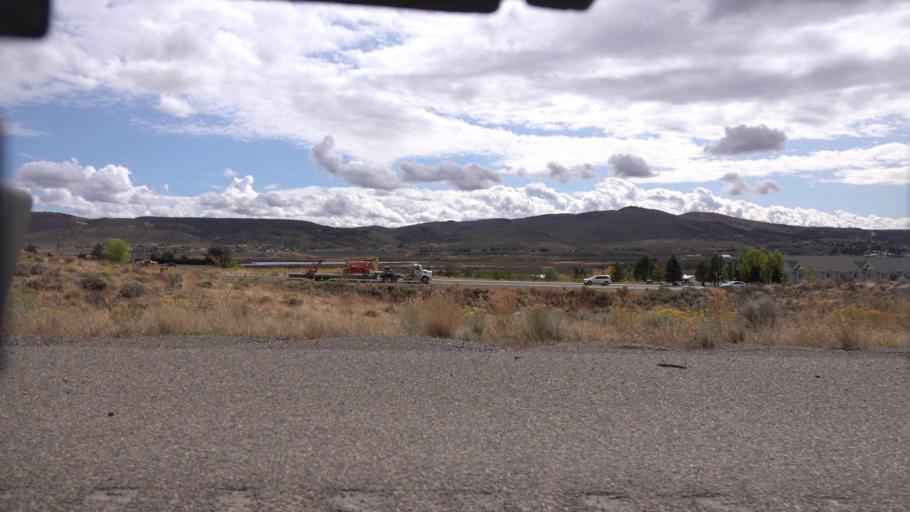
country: US
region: Nevada
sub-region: Elko County
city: Elko
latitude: 40.8575
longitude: -115.7413
